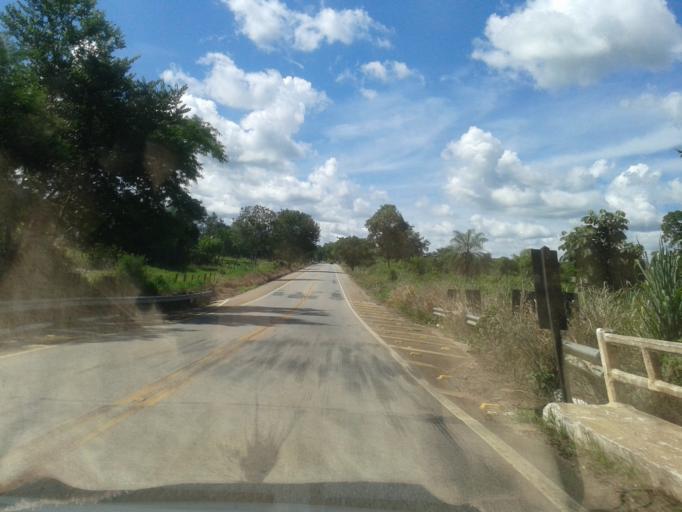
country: BR
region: Goias
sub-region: Itapuranga
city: Itapuranga
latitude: -15.6357
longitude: -50.2285
